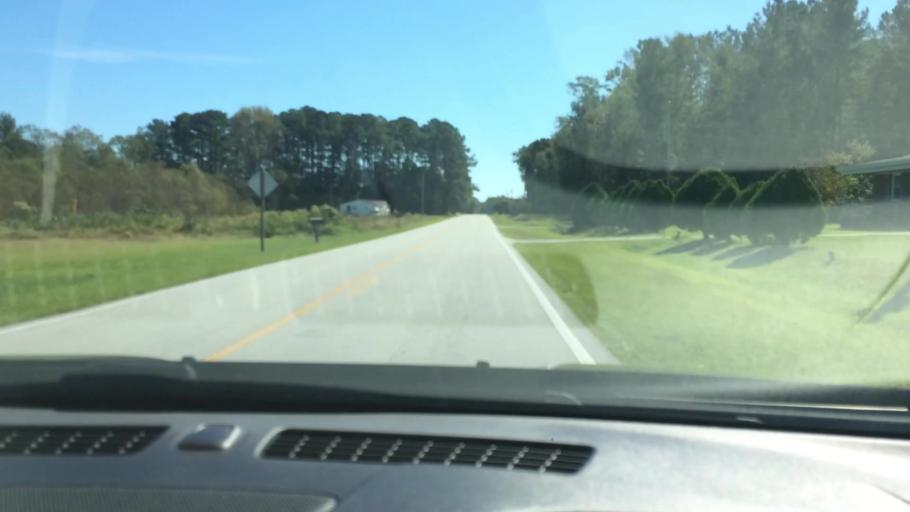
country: US
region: North Carolina
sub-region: Pitt County
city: Grifton
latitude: 35.3413
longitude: -77.3138
